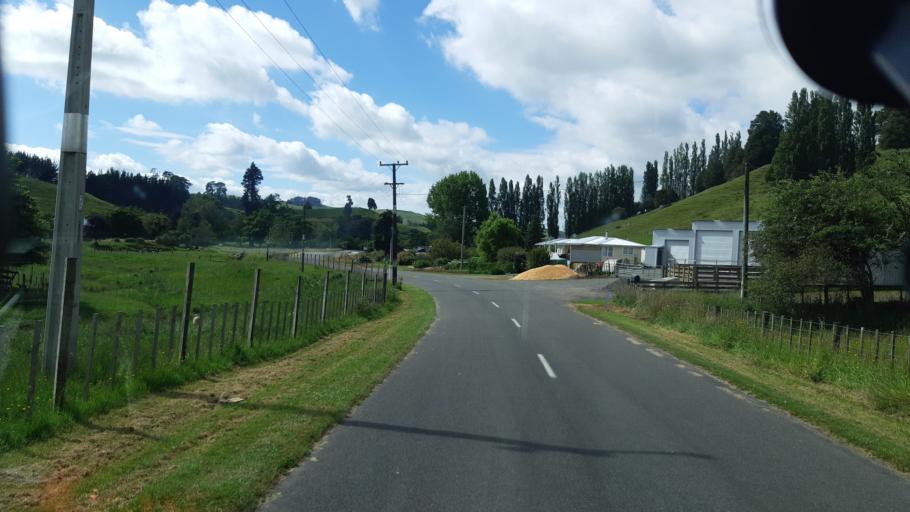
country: NZ
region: Manawatu-Wanganui
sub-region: Rangitikei District
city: Bulls
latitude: -39.9252
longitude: 175.5603
